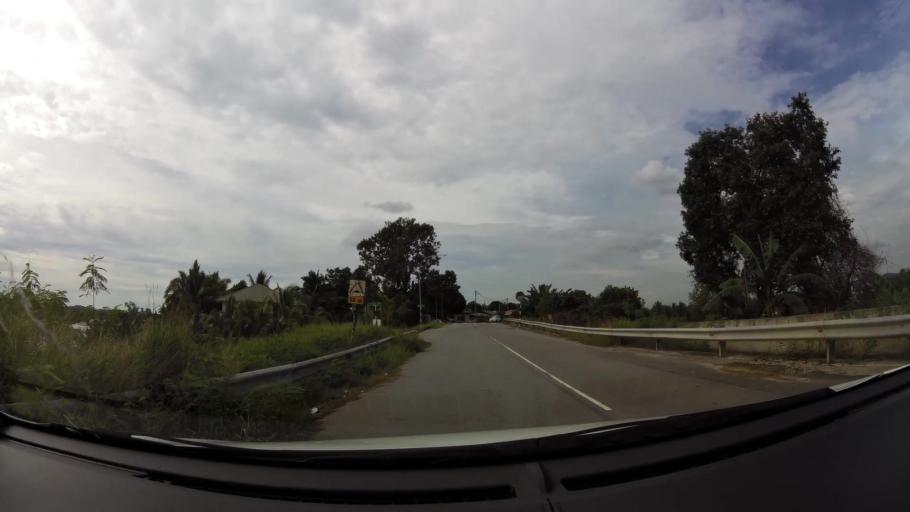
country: BN
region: Brunei and Muara
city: Bandar Seri Begawan
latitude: 4.8944
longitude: 114.8954
